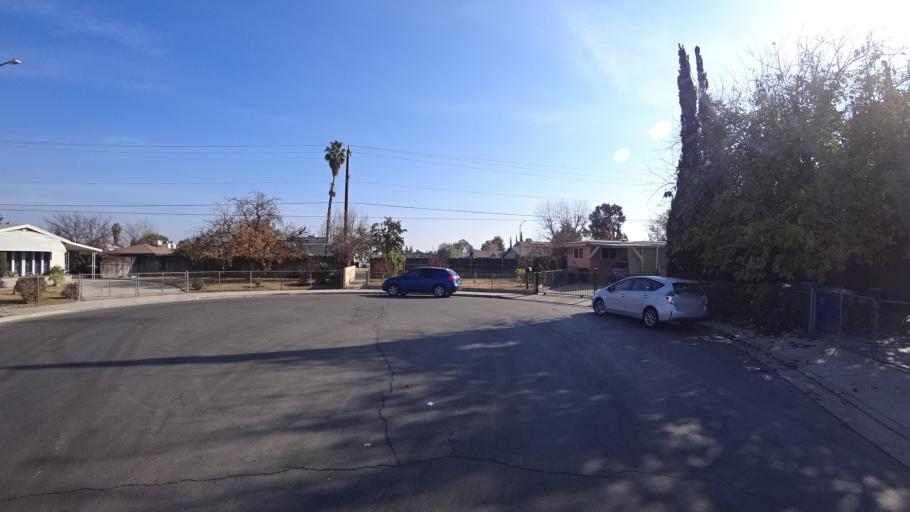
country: US
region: California
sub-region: Kern County
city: Greenfield
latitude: 35.3057
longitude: -119.0306
